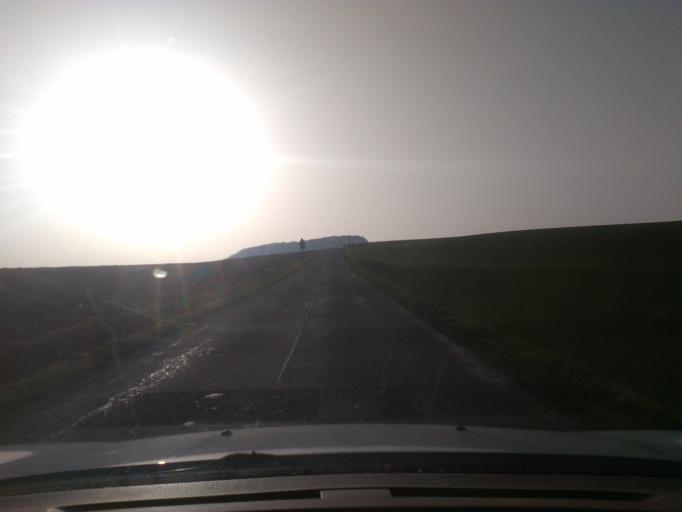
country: FR
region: Lorraine
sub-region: Departement des Vosges
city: Vittel
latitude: 48.2732
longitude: 6.0223
